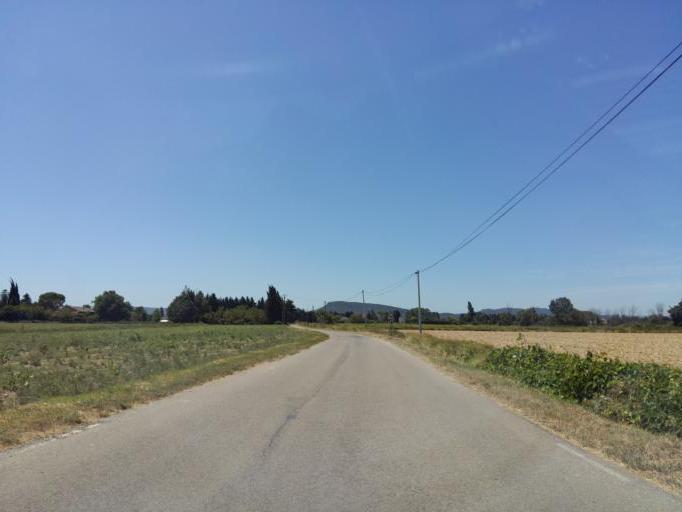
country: FR
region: Provence-Alpes-Cote d'Azur
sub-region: Departement du Vaucluse
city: Piolenc
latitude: 44.1548
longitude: 4.7703
